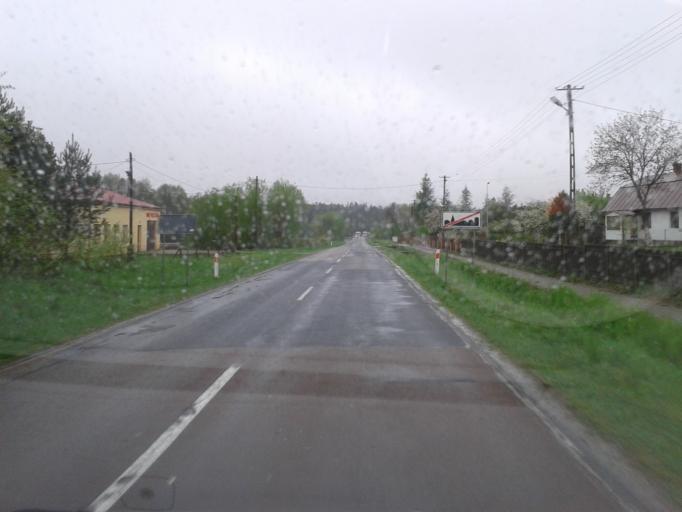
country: PL
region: Subcarpathian Voivodeship
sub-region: Powiat lubaczowski
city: Narol
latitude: 50.3107
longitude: 23.2405
